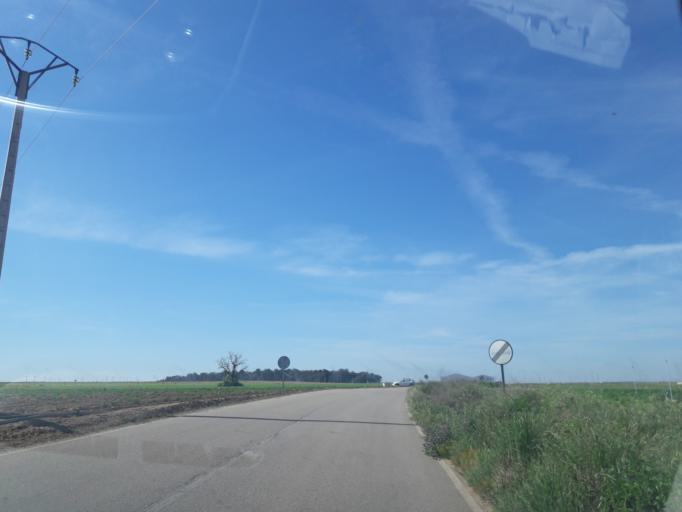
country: ES
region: Castille and Leon
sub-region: Provincia de Salamanca
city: Villoruela
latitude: 41.0410
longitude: -5.3868
